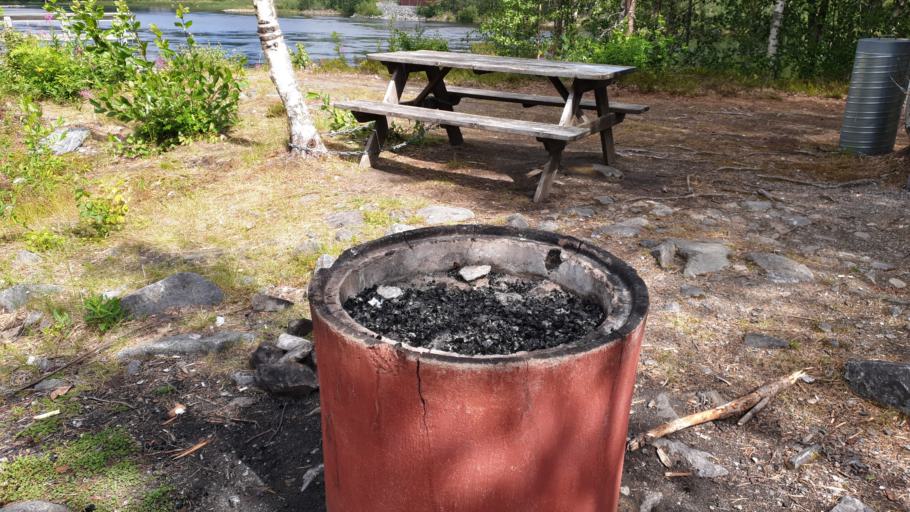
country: SE
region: Vaesterbotten
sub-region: Umea Kommun
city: Roback
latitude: 63.8315
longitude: 20.1285
